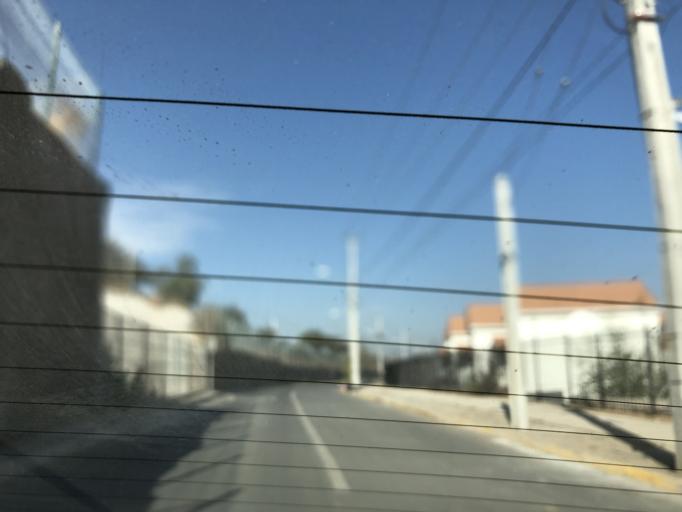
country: CL
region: Santiago Metropolitan
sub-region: Provincia de Cordillera
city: Puente Alto
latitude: -33.5719
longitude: -70.5395
